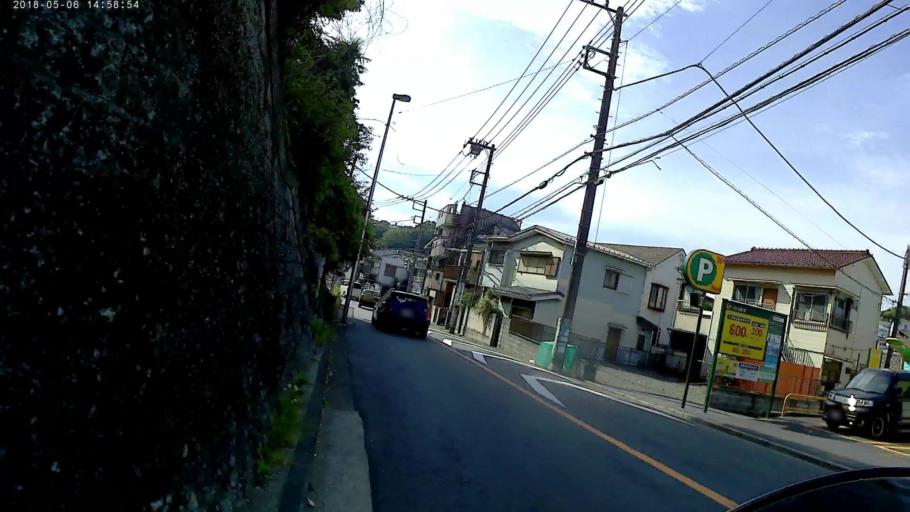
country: JP
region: Kanagawa
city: Yokohama
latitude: 35.4184
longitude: 139.6161
